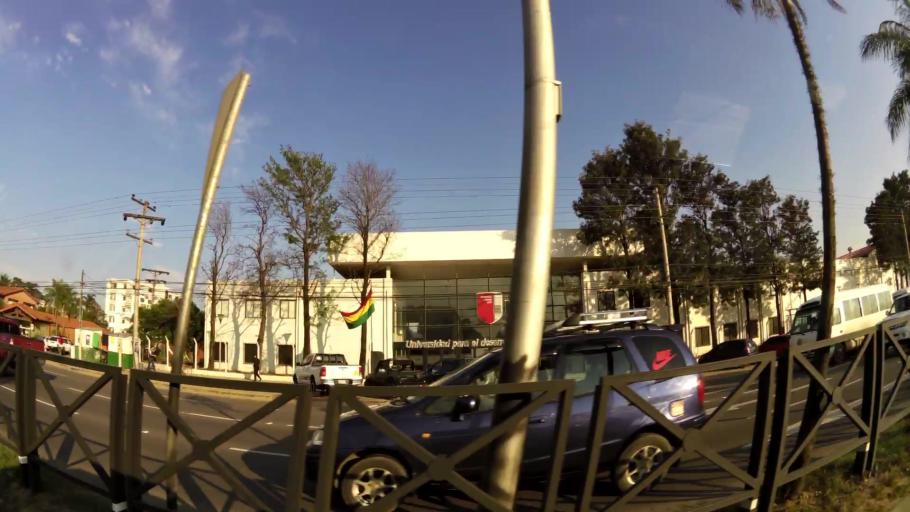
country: BO
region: Santa Cruz
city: Santa Cruz de la Sierra
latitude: -17.7345
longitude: -63.1692
